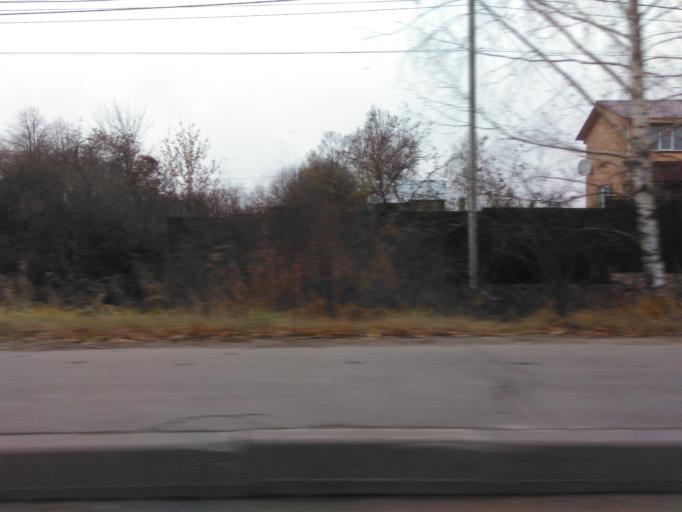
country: RU
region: Moskovskaya
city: Sofrino
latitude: 56.1166
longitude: 37.9611
